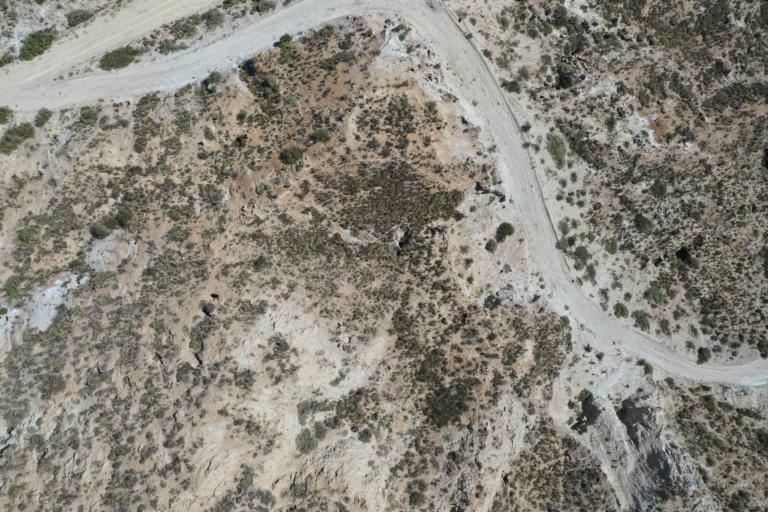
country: BO
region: La Paz
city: La Paz
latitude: -16.5531
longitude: -68.1241
